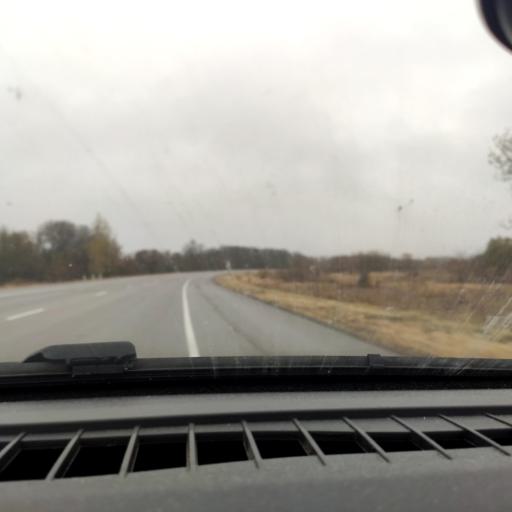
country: RU
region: Voronezj
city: Kolodeznyy
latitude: 51.3138
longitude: 39.0298
